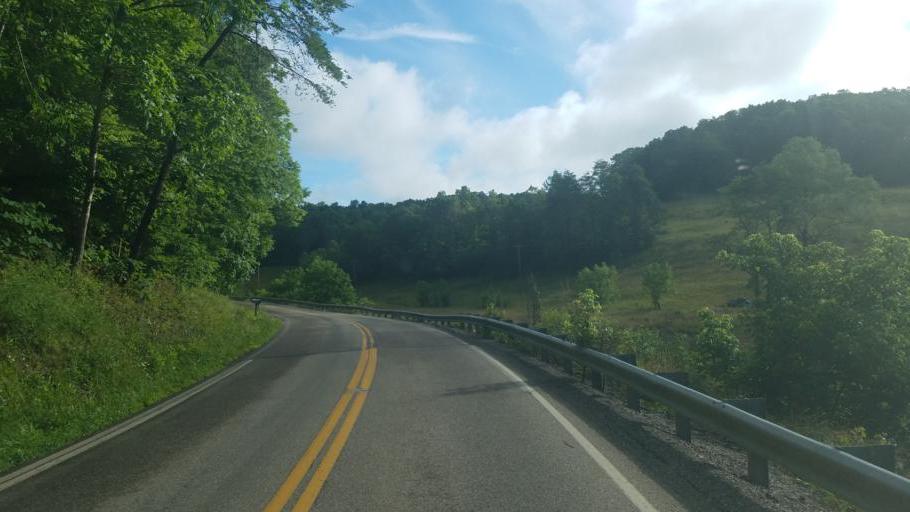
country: US
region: Ohio
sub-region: Gallia County
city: Gallipolis
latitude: 38.7690
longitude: -82.3553
